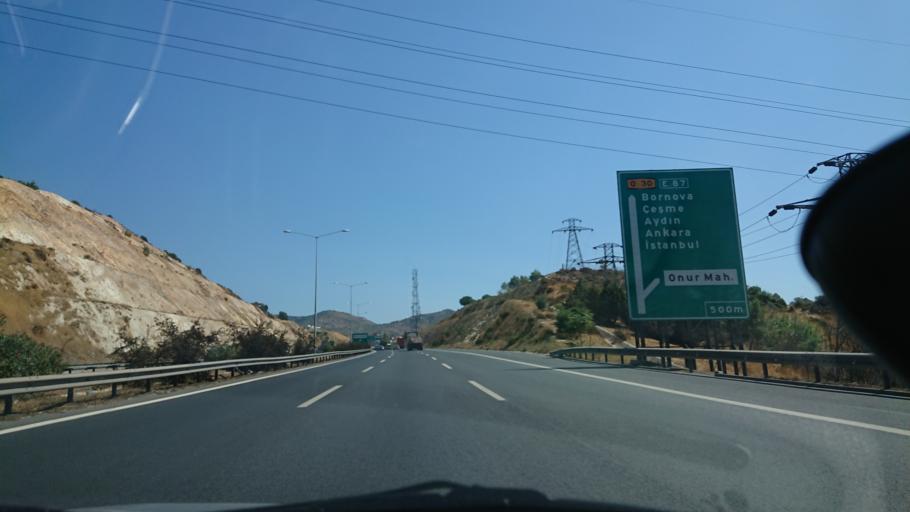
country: TR
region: Izmir
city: Karsiyaka
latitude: 38.4860
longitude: 27.1213
